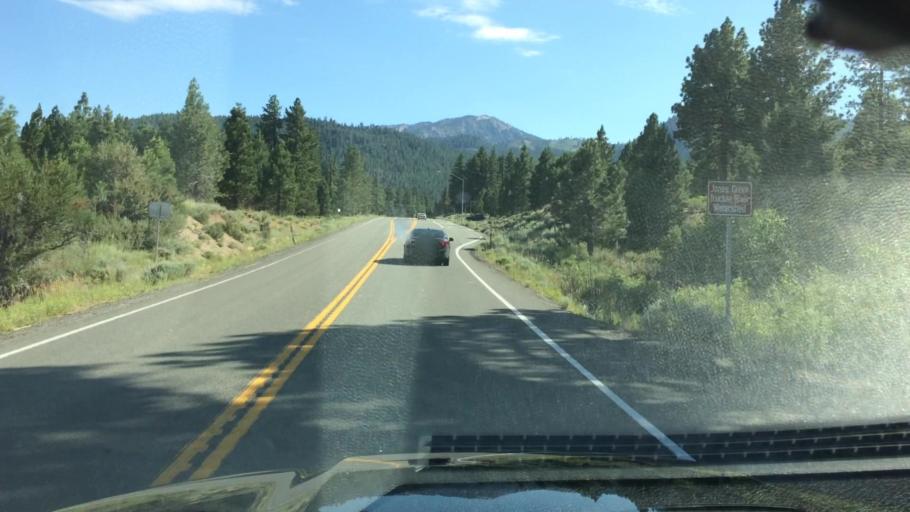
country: US
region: Nevada
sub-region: Washoe County
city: Mogul
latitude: 39.3652
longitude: -119.8493
